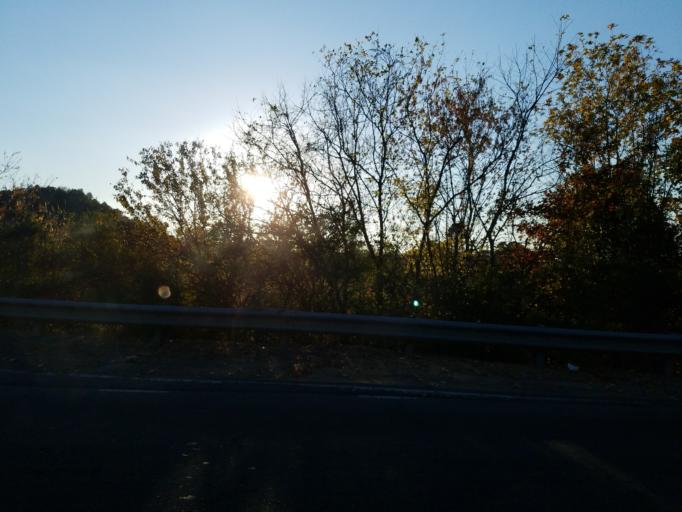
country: US
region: Georgia
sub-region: Gordon County
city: Calhoun
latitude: 34.4817
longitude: -84.9529
